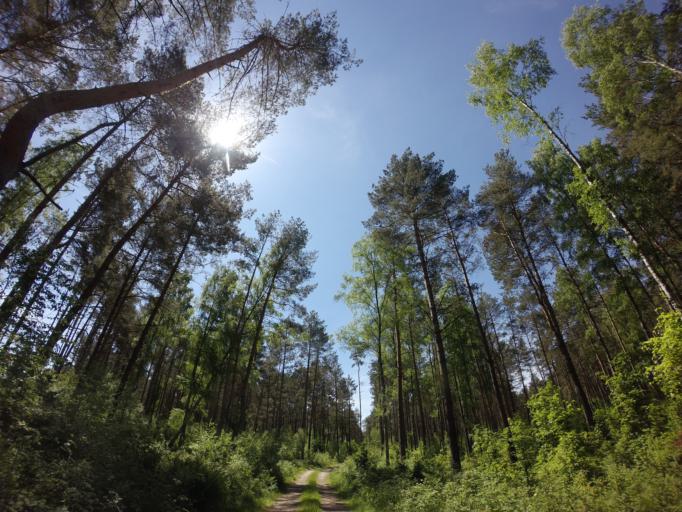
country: PL
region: West Pomeranian Voivodeship
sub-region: Powiat choszczenski
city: Drawno
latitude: 53.2728
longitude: 15.7370
